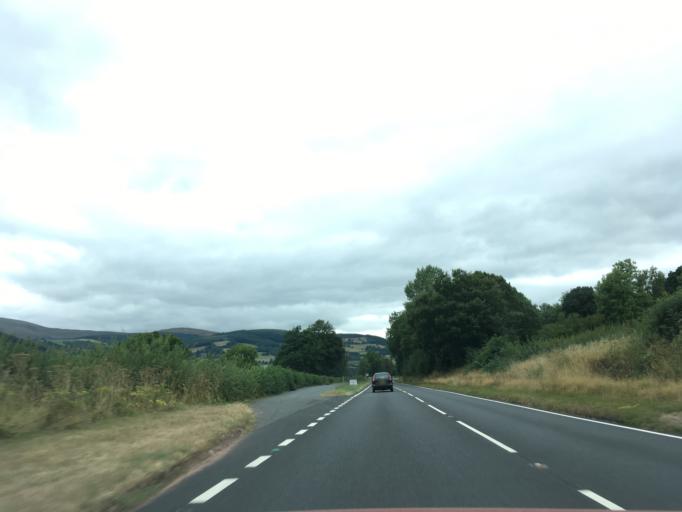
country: GB
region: Wales
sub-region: Blaenau Gwent
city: Brynmawr
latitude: 51.8938
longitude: -3.2600
